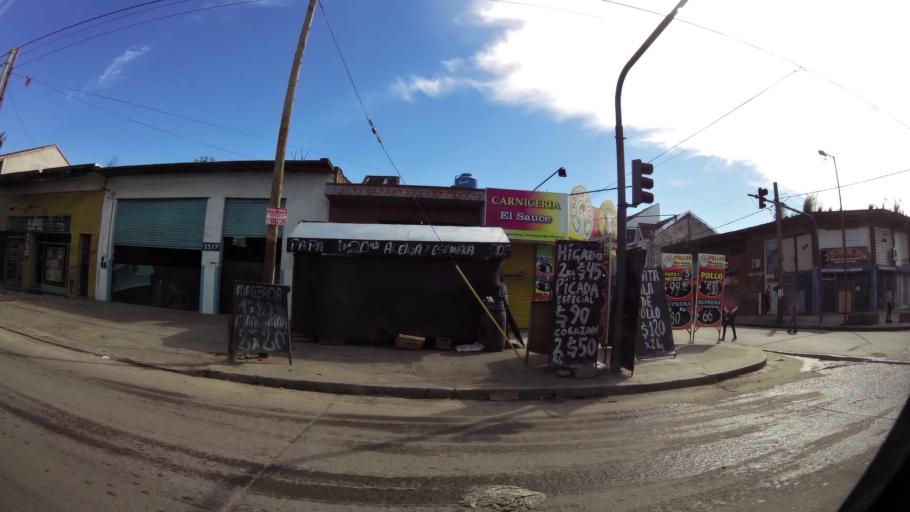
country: AR
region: Buenos Aires
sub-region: Partido de Almirante Brown
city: Adrogue
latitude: -34.7731
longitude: -58.3125
